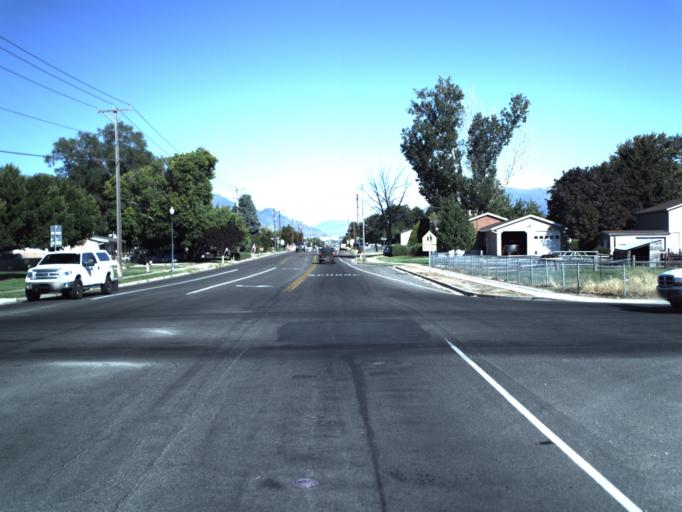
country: US
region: Utah
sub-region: Davis County
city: West Point
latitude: 41.1398
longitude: -112.0840
